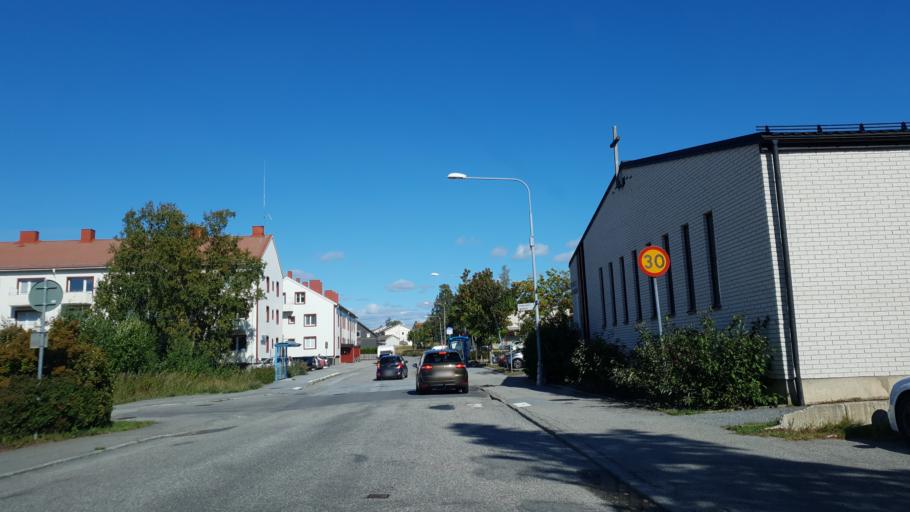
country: SE
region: Vaesterbotten
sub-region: Umea Kommun
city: Holmsund
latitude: 63.7073
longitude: 20.3640
